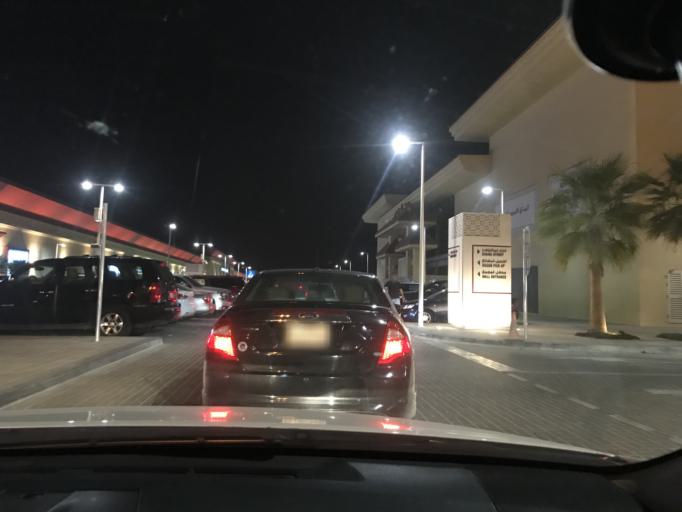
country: BH
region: Muharraq
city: Al Muharraq
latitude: 26.3052
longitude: 50.6273
